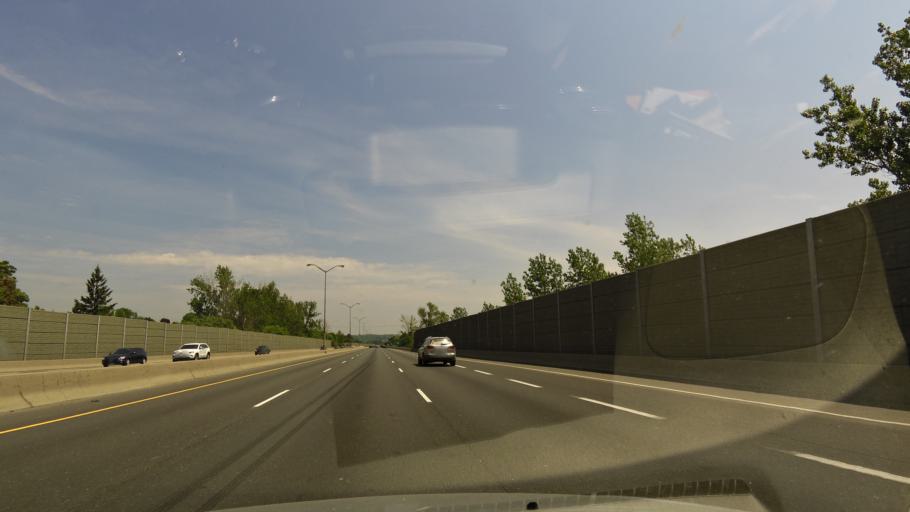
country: CA
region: Ontario
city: Oshawa
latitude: 43.8839
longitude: -78.8453
